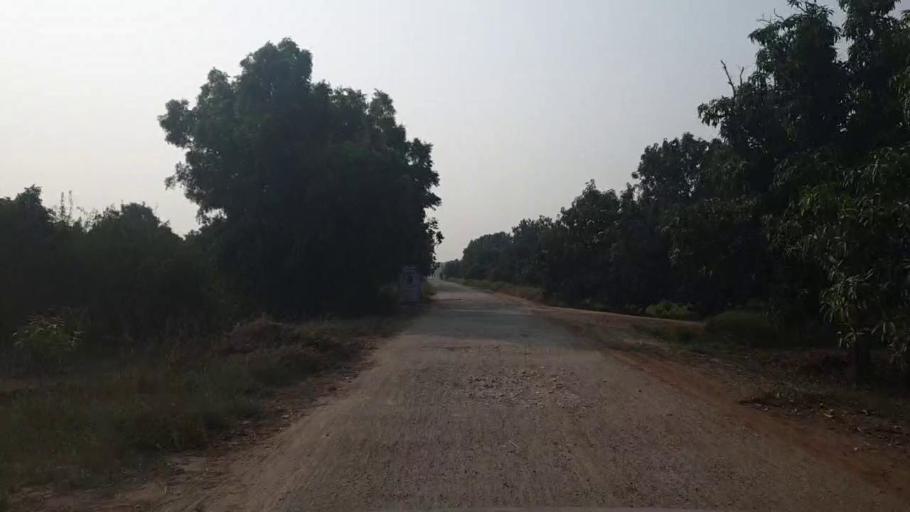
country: PK
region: Sindh
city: Tando Jam
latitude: 25.3296
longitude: 68.5180
